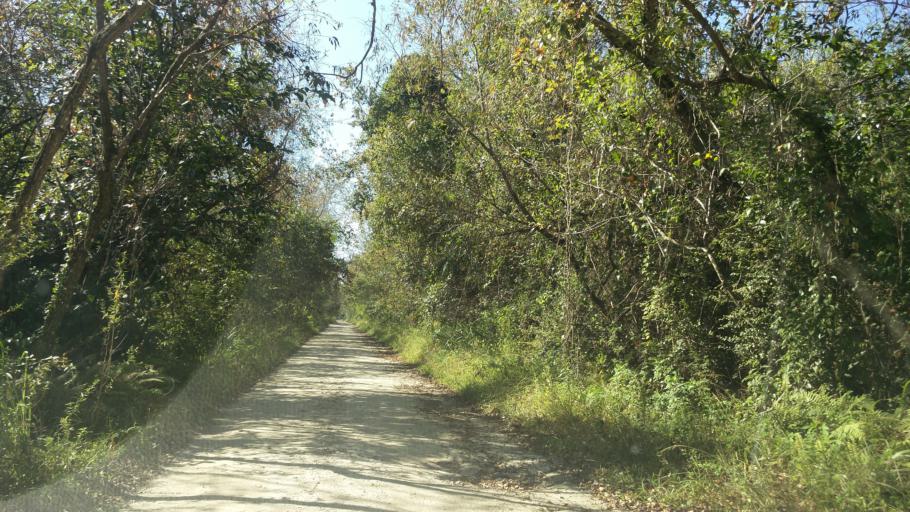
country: US
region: Florida
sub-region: Collier County
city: Lely Resort
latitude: 25.9799
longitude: -81.4049
